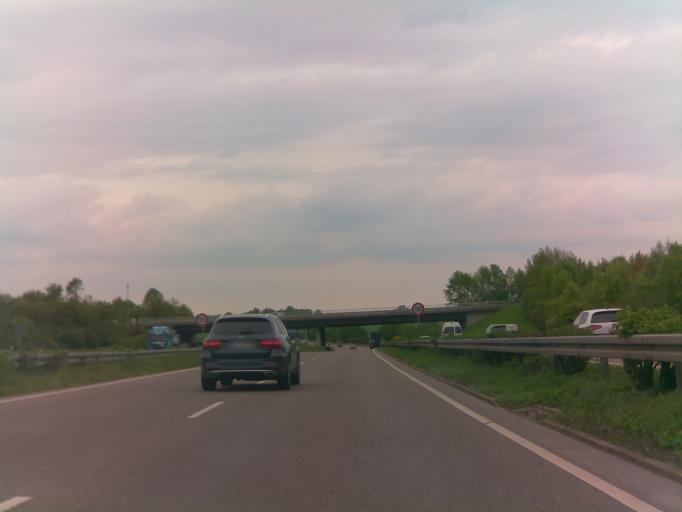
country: DE
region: Baden-Wuerttemberg
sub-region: Regierungsbezirk Stuttgart
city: Ehningen
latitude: 48.6861
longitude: 8.9691
